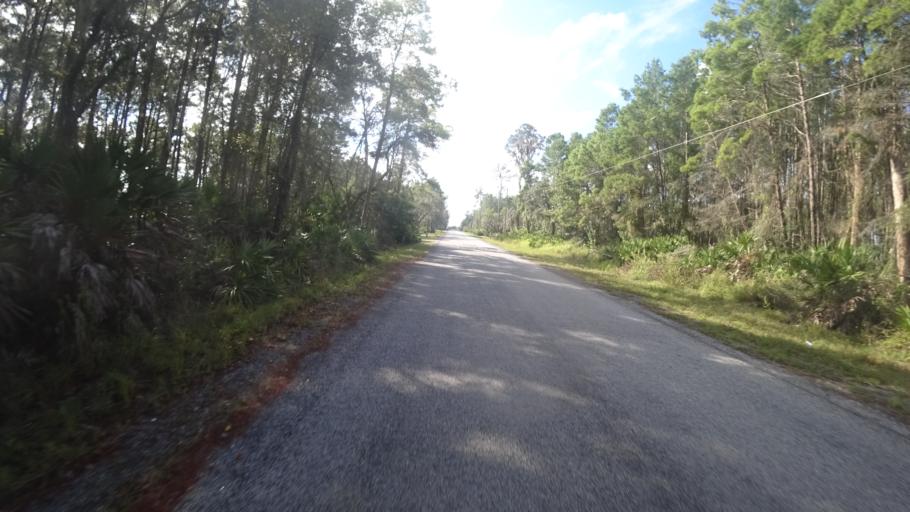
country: US
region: Florida
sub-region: Hillsborough County
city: Wimauma
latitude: 27.4573
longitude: -82.1370
